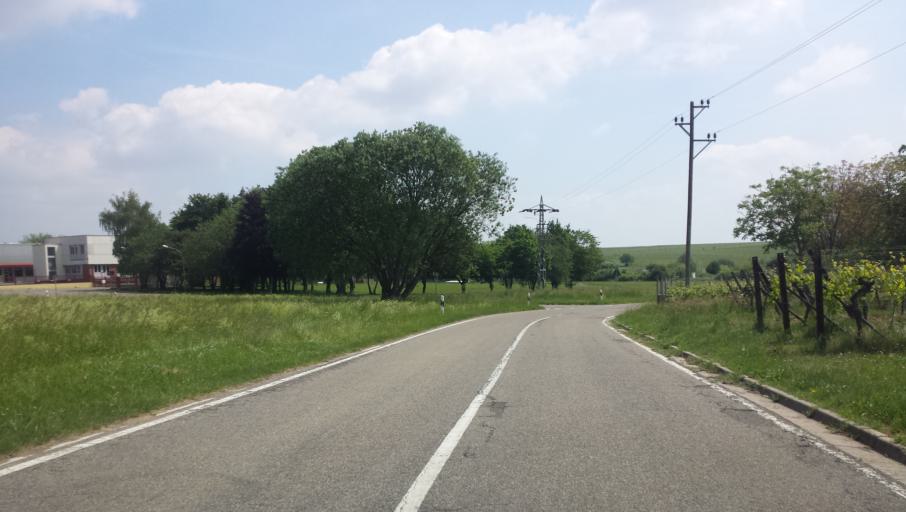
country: DE
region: Rheinland-Pfalz
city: Gocklingen
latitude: 49.1721
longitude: 8.0402
